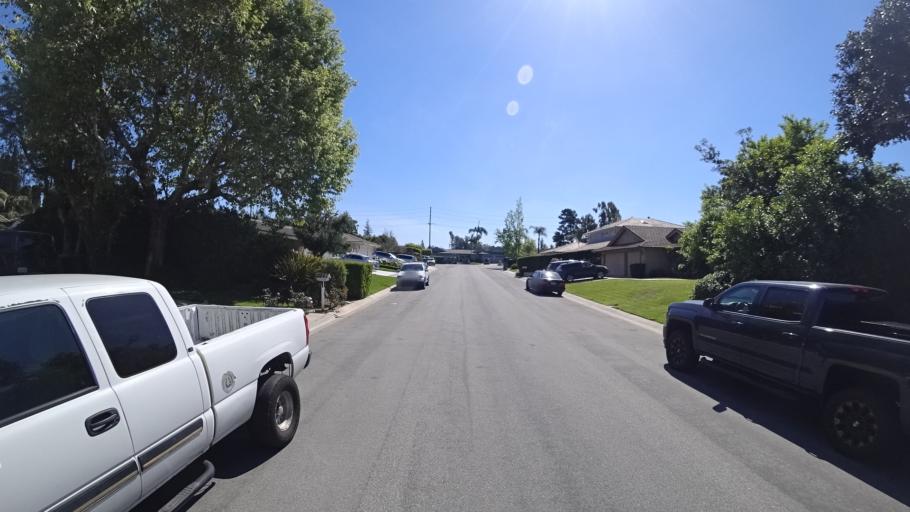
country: US
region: California
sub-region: Orange County
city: Villa Park
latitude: 33.8172
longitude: -117.8214
